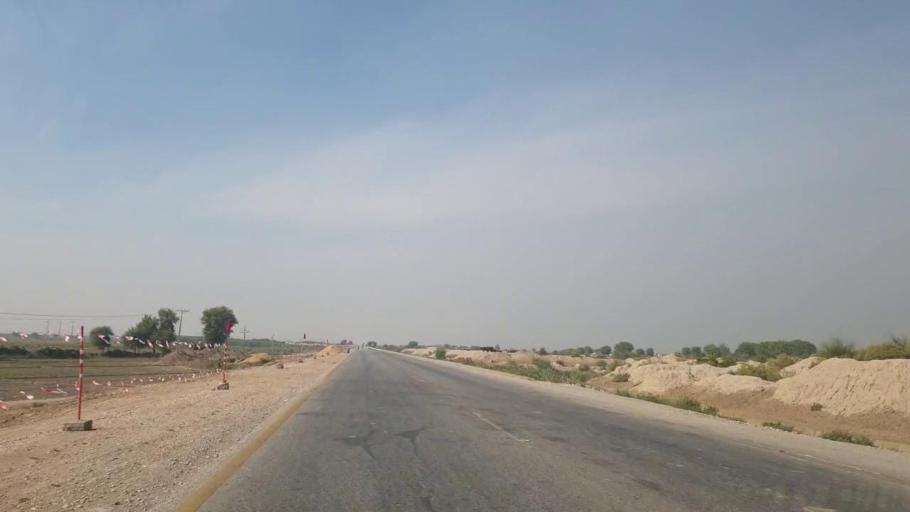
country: PK
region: Sindh
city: Sann
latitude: 25.9919
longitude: 68.1739
